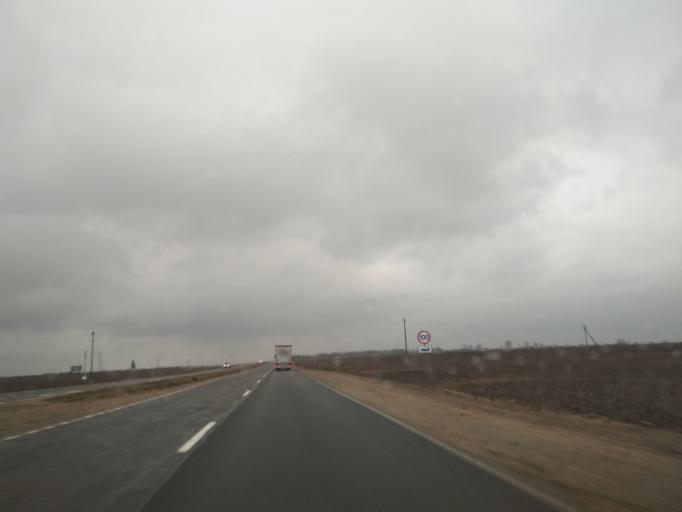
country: BY
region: Minsk
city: Dukora
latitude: 53.6427
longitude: 27.9921
